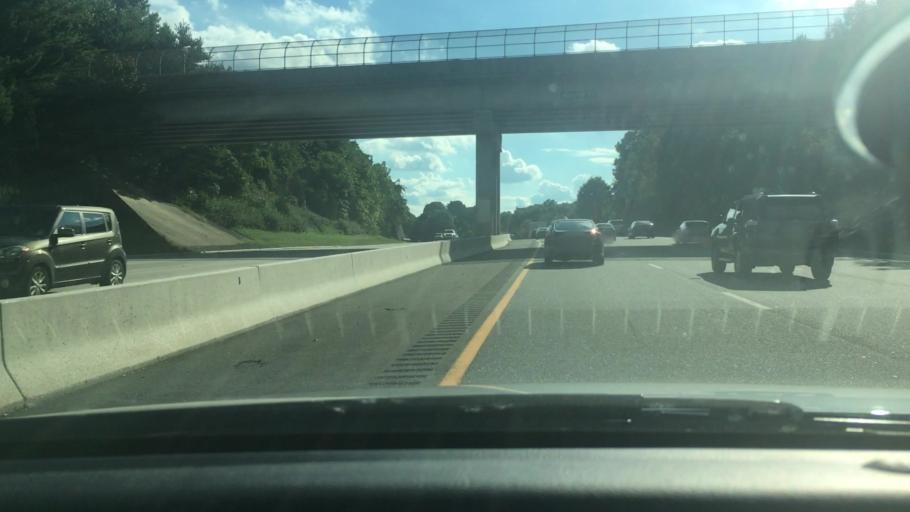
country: US
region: New Jersey
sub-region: Morris County
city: Lincoln Park
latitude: 40.9345
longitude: -74.3542
